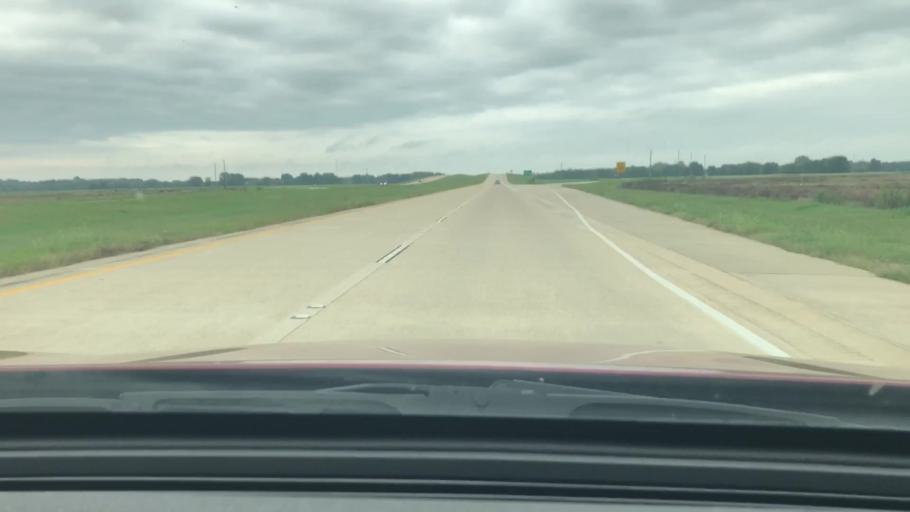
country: US
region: Louisiana
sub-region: Caddo Parish
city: Oil City
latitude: 32.7086
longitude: -93.8645
